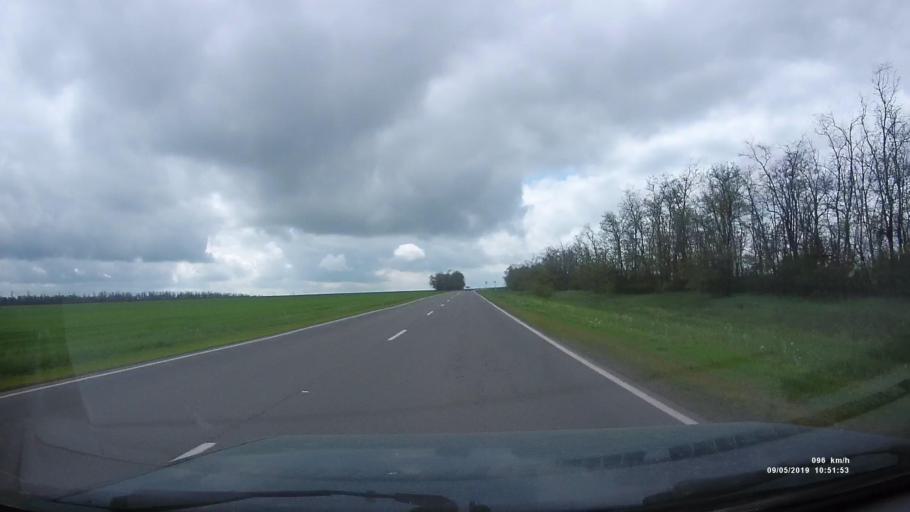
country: RU
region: Rostov
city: Peshkovo
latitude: 46.9080
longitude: 39.3547
